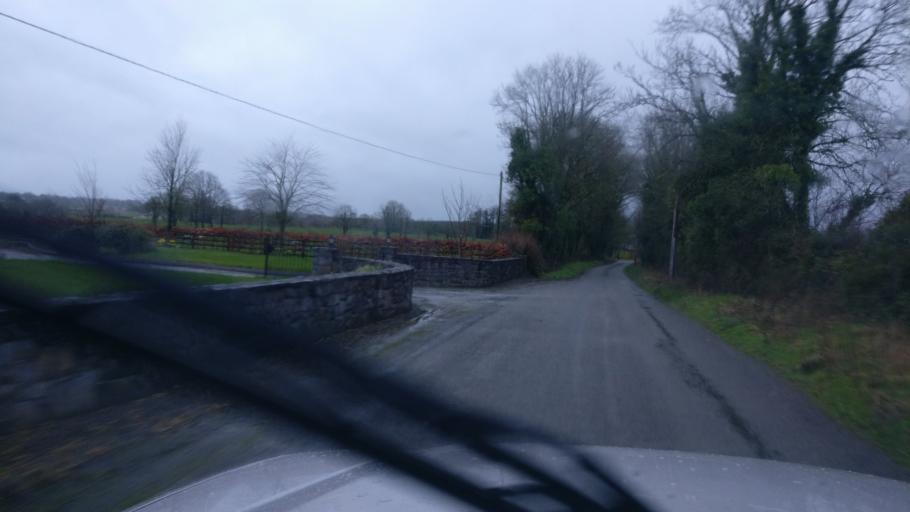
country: IE
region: Connaught
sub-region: County Galway
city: Loughrea
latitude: 53.2570
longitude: -8.3950
